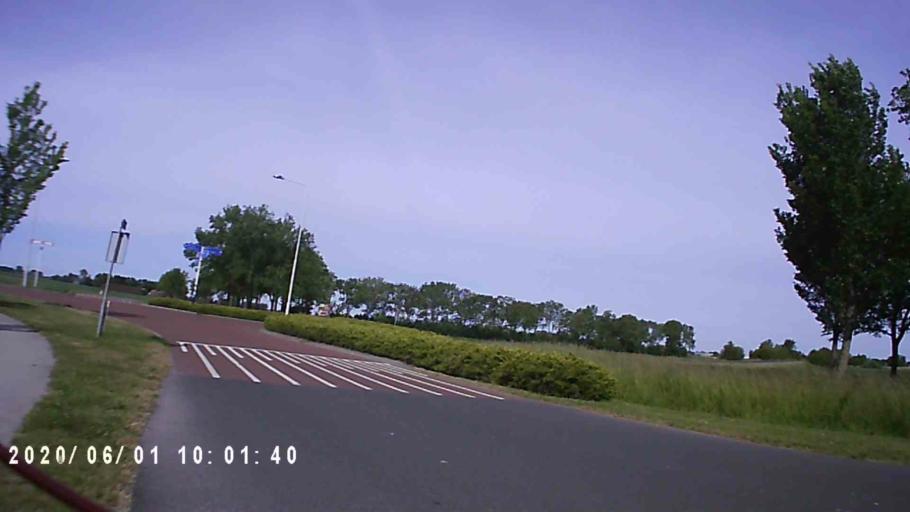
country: NL
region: Friesland
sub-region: Menameradiel
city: Berltsum
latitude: 53.2405
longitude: 5.6363
